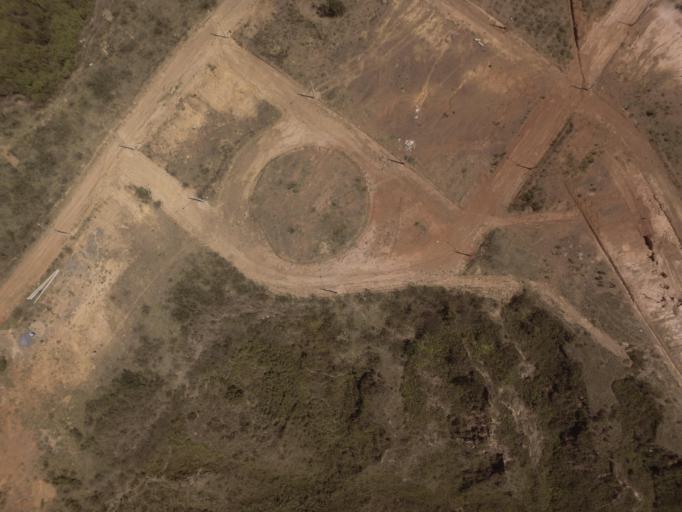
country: BR
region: Minas Gerais
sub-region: Tiradentes
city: Tiradentes
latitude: -21.0506
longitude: -44.0847
